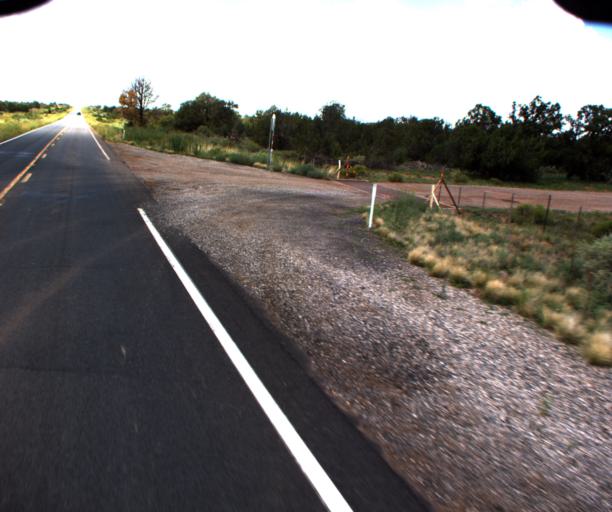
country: US
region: Arizona
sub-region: Coconino County
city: Parks
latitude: 35.6093
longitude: -112.0589
